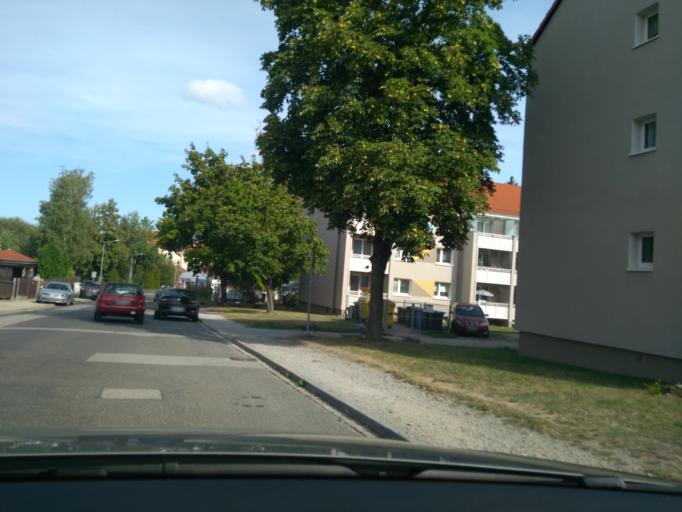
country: DE
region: Saxony
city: Bautzen
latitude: 51.1670
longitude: 14.4403
